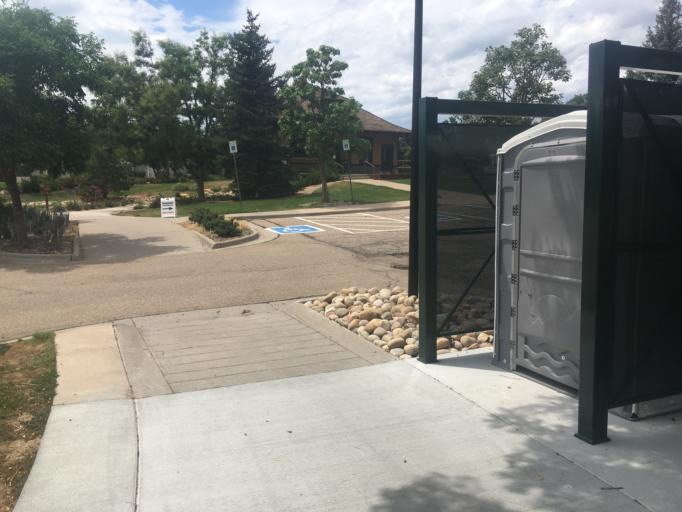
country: US
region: Colorado
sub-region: Broomfield County
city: Broomfield
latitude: 39.9301
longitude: -105.0939
